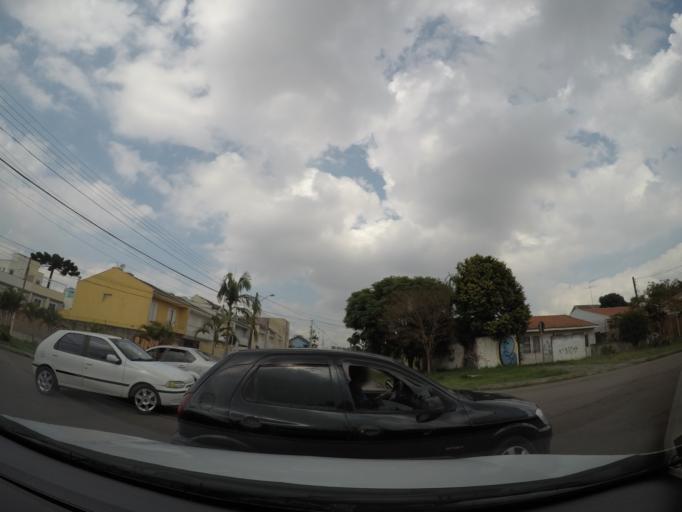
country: BR
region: Parana
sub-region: Sao Jose Dos Pinhais
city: Sao Jose dos Pinhais
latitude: -25.5011
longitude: -49.2432
